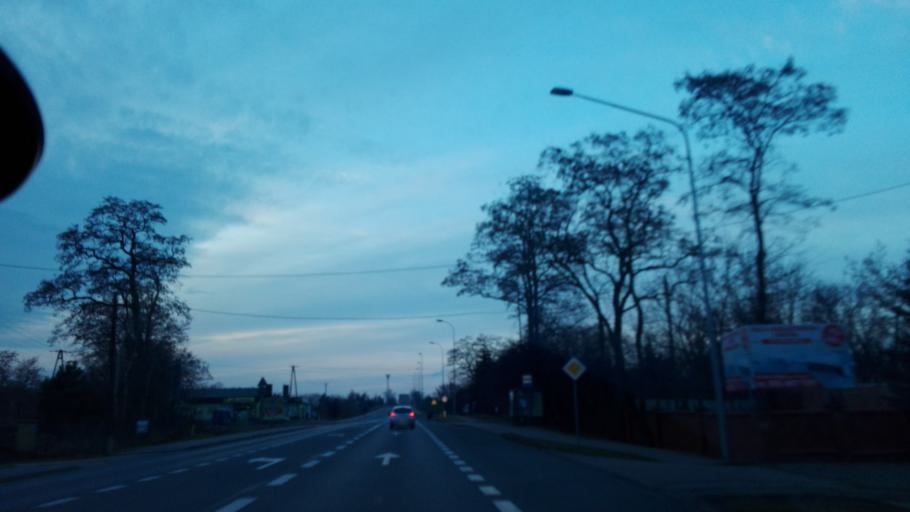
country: PL
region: Masovian Voivodeship
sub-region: Powiat siedlecki
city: Skorzec
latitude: 52.1763
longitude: 22.1897
